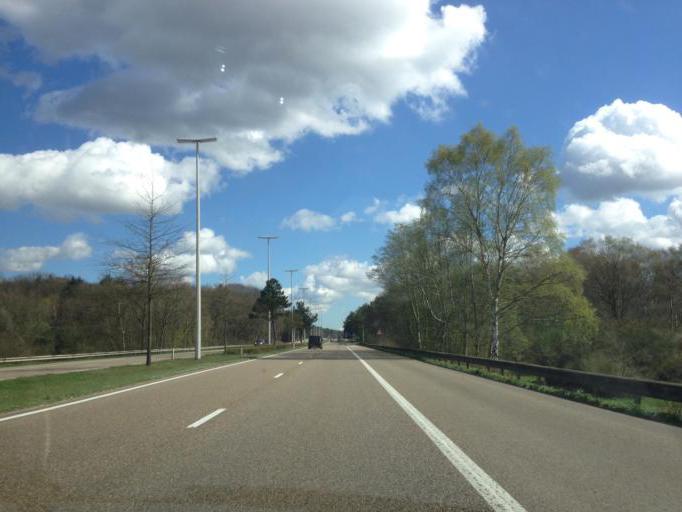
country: BE
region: Flanders
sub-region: Provincie Limburg
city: Genk
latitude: 50.9741
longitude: 5.5418
